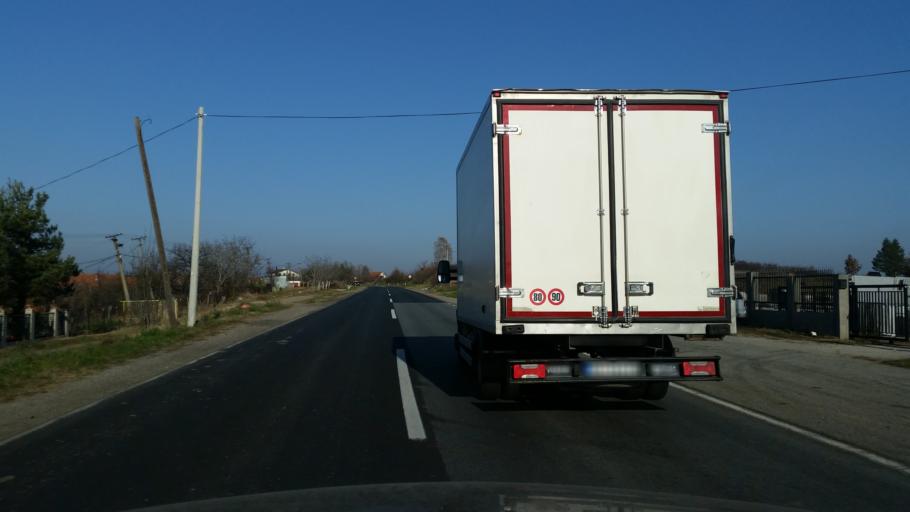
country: RS
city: Stepojevac
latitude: 44.5602
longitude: 20.3005
